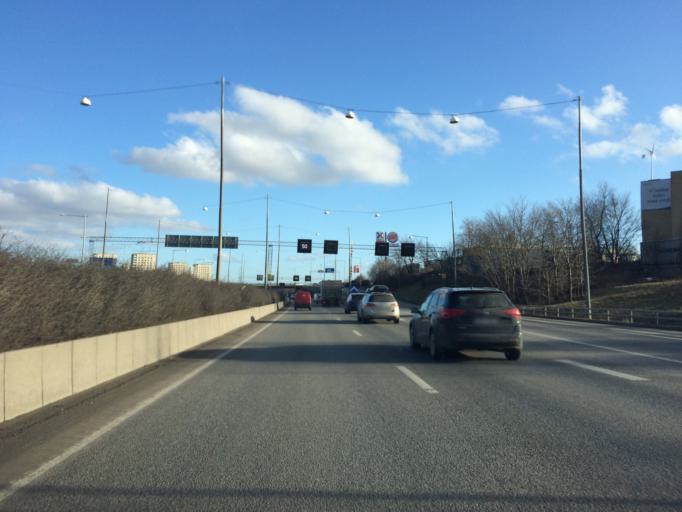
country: SE
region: Stockholm
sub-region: Stockholms Kommun
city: Arsta
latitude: 59.2976
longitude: 18.0309
